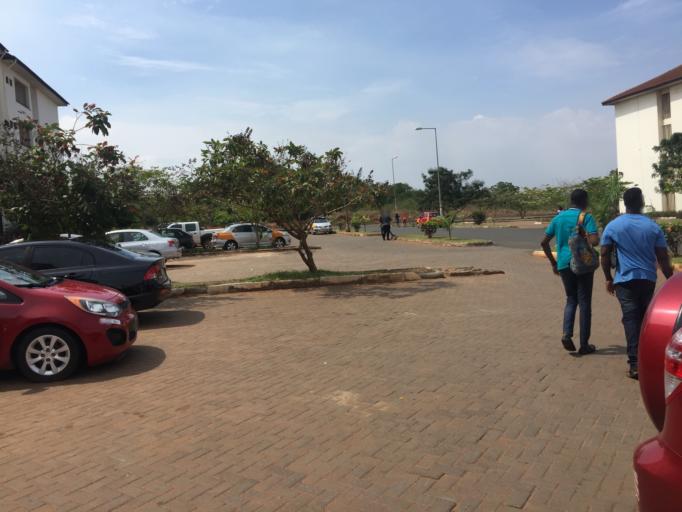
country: GH
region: Greater Accra
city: Medina Estates
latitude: 5.6357
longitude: -0.1881
